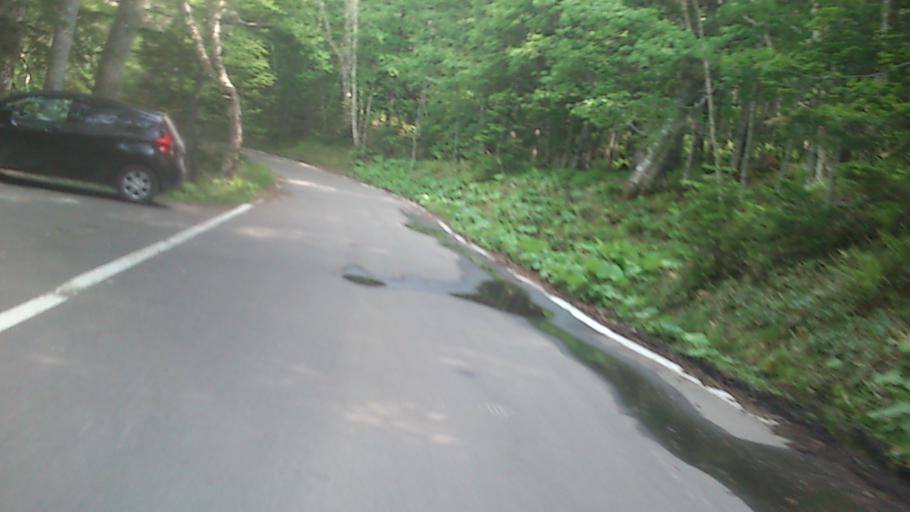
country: JP
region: Hokkaido
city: Kitami
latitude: 43.3826
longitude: 143.9652
